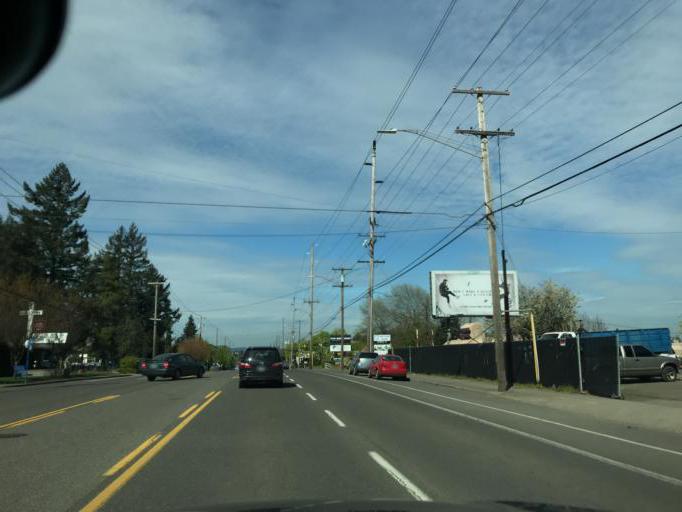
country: US
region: Oregon
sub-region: Multnomah County
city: Lents
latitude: 45.5043
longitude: -122.5572
